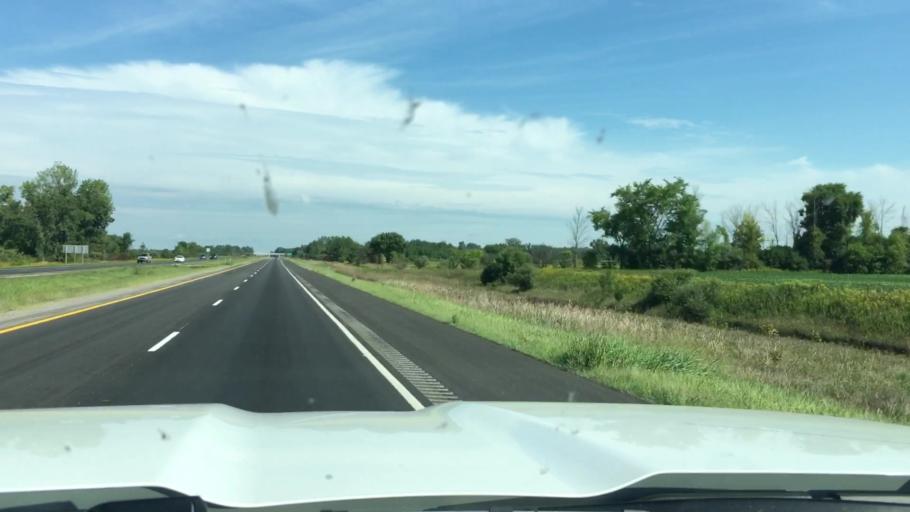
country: US
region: Michigan
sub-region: Saginaw County
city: Freeland
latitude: 43.5527
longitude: -84.1387
